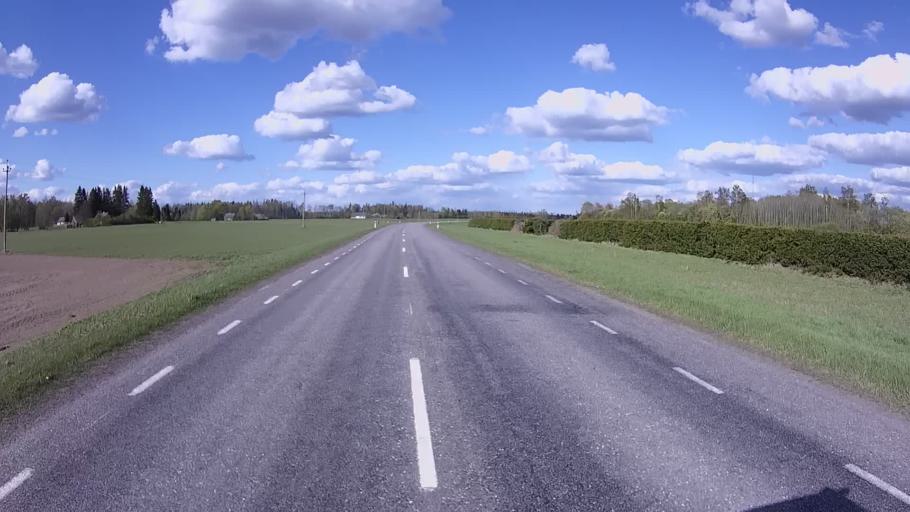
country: EE
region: Jogevamaa
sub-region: Poltsamaa linn
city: Poltsamaa
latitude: 58.6941
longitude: 26.1349
